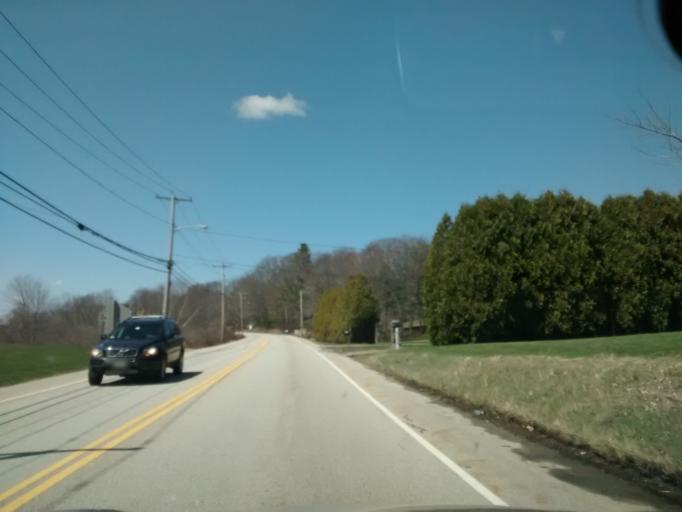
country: US
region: Massachusetts
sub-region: Worcester County
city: Oxford
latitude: 42.1138
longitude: -71.8428
